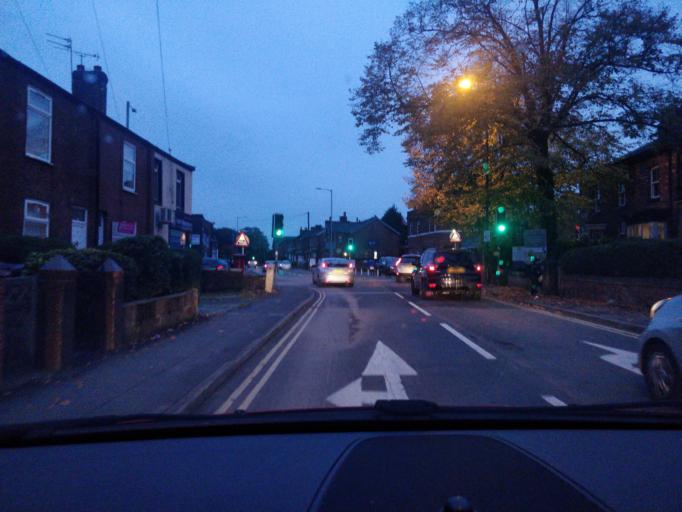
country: GB
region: England
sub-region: Lancashire
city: Ormskirk
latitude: 53.5671
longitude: -2.8815
